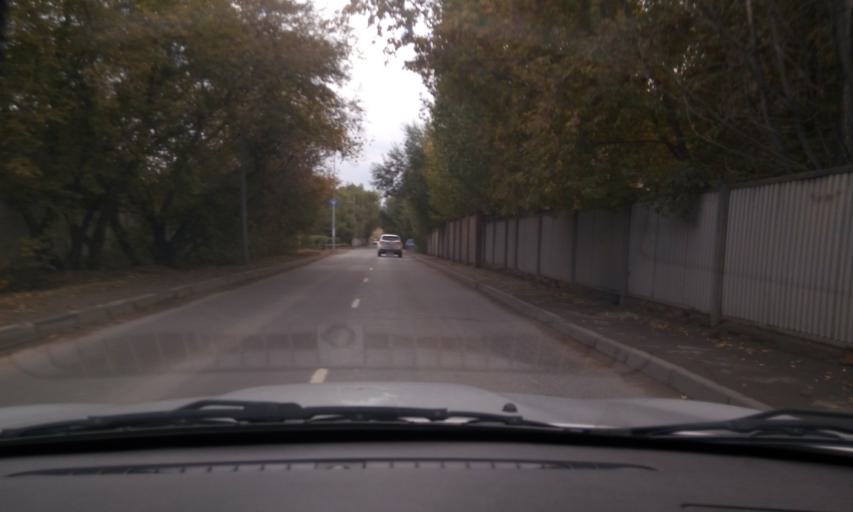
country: KZ
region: Astana Qalasy
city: Astana
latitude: 51.1420
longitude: 71.4320
